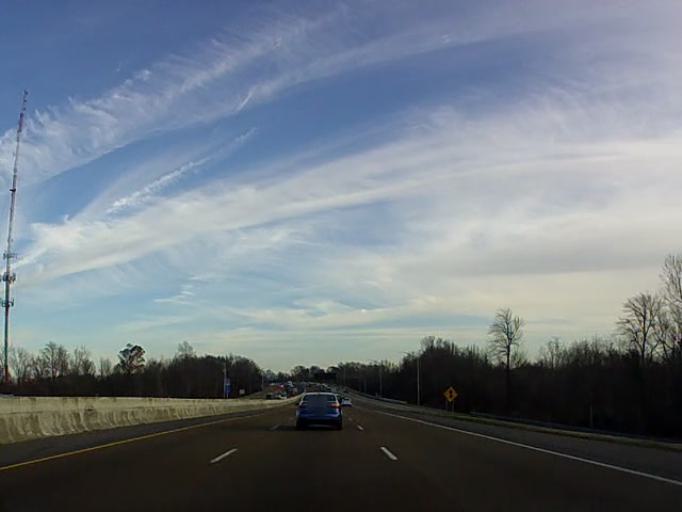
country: US
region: Tennessee
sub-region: Shelby County
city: Germantown
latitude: 35.0729
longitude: -89.8584
